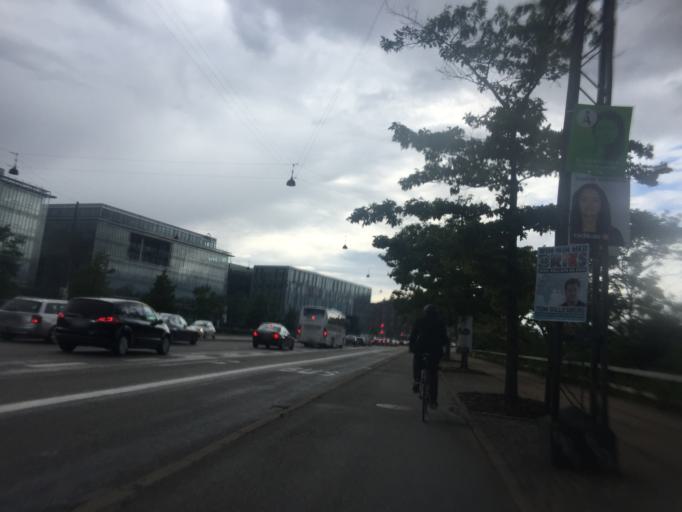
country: DK
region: Capital Region
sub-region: Kobenhavn
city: Christianshavn
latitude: 55.6682
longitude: 12.5850
